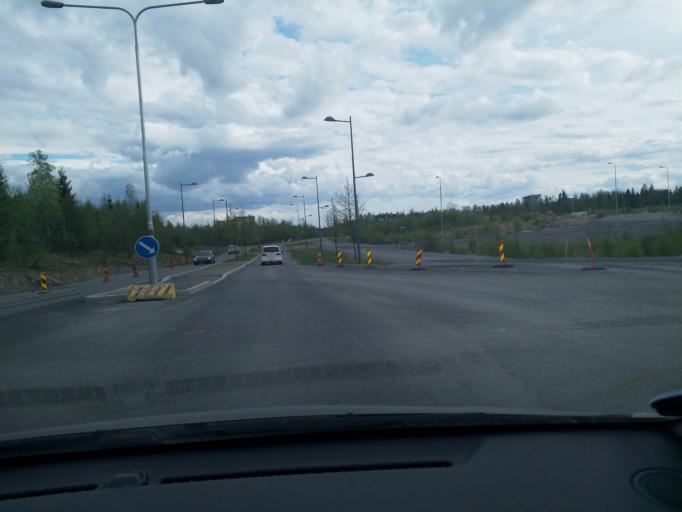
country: FI
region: Pirkanmaa
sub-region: Tampere
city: Tampere
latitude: 61.4437
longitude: 23.8066
